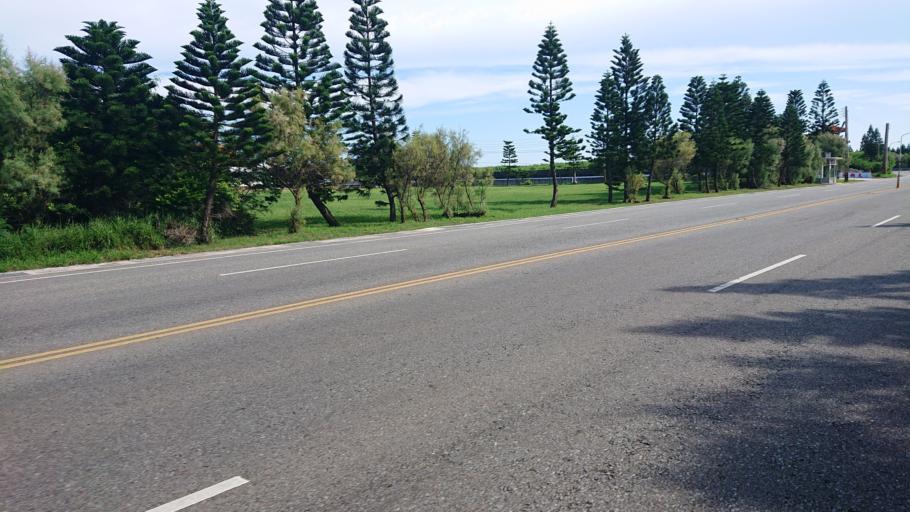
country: TW
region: Taiwan
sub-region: Penghu
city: Ma-kung
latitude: 23.5475
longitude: 119.6086
